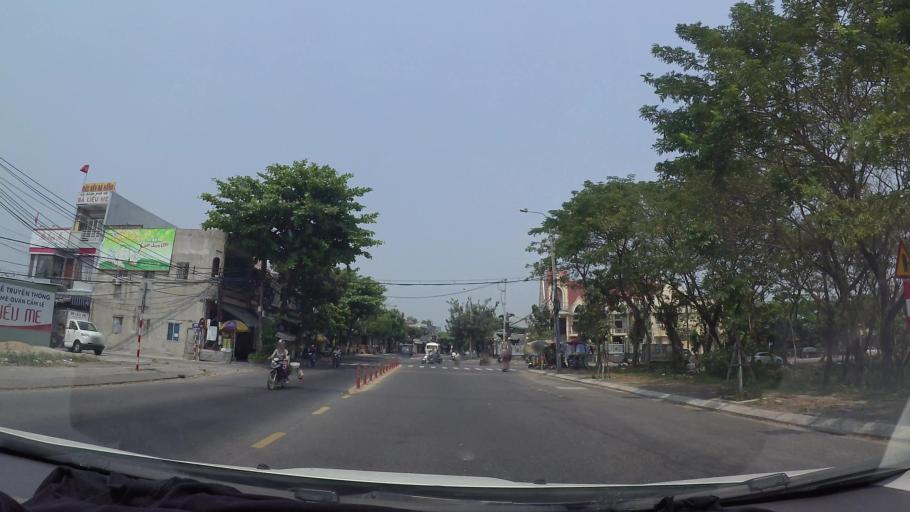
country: VN
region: Da Nang
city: Cam Le
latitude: 16.0111
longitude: 108.2059
